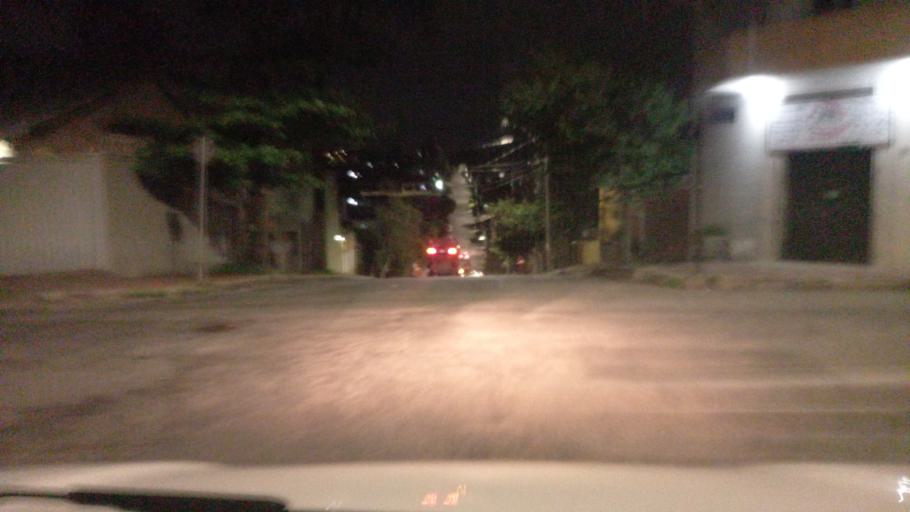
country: BR
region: Minas Gerais
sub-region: Belo Horizonte
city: Belo Horizonte
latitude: -19.8904
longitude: -43.9390
